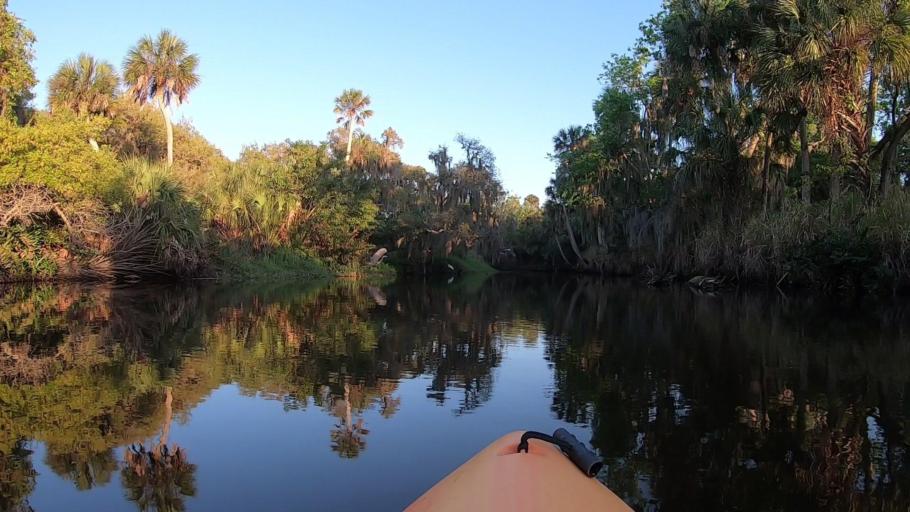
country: US
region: Florida
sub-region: Manatee County
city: Memphis
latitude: 27.5912
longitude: -82.5512
